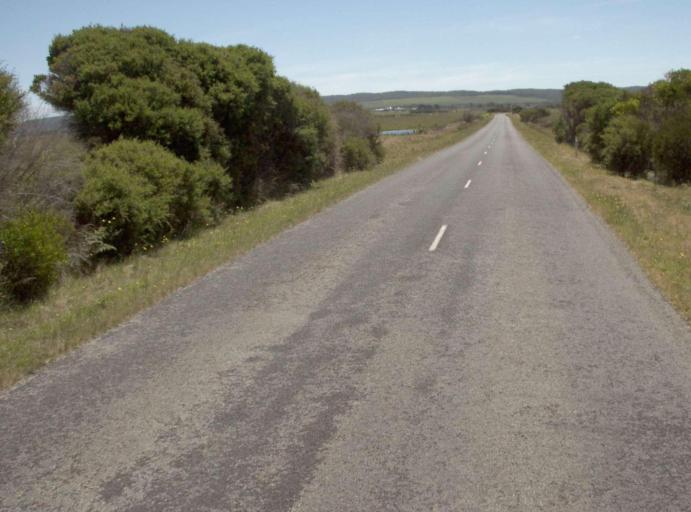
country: AU
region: Victoria
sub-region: Bass Coast
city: North Wonthaggi
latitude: -38.8097
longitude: 146.0919
